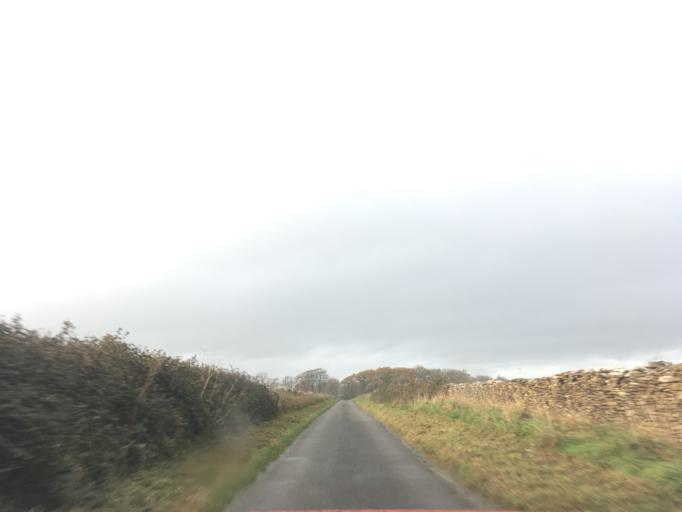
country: GB
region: England
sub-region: South Gloucestershire
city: Cold Ashton
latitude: 51.4697
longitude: -2.3613
